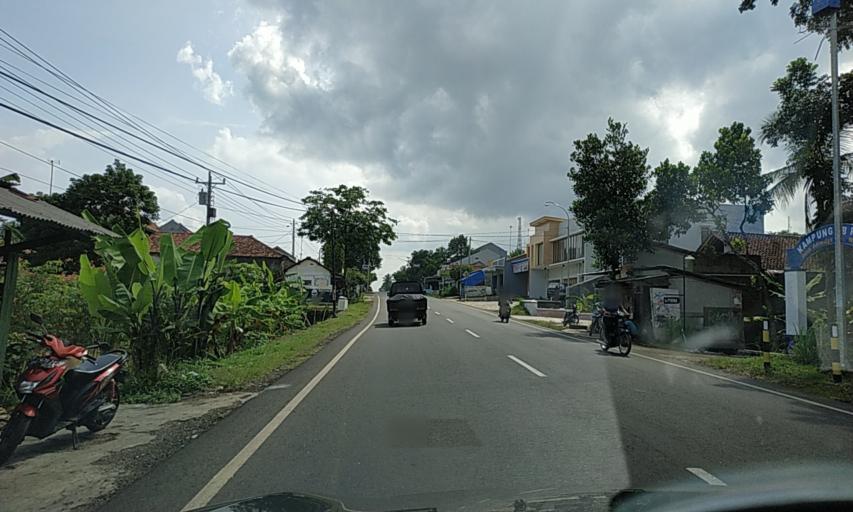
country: ID
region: Central Java
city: Cihandiwung Lor
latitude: -7.3355
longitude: 108.6928
